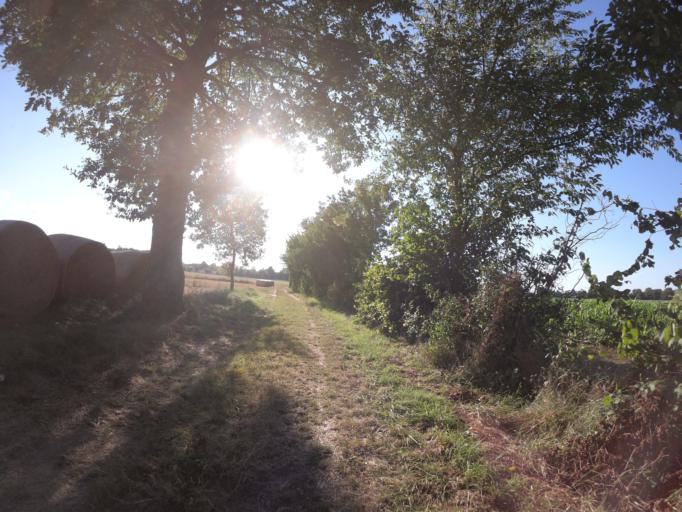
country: FR
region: Midi-Pyrenees
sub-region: Departement de l'Ariege
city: La Tour-du-Crieu
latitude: 43.0993
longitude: 1.7387
